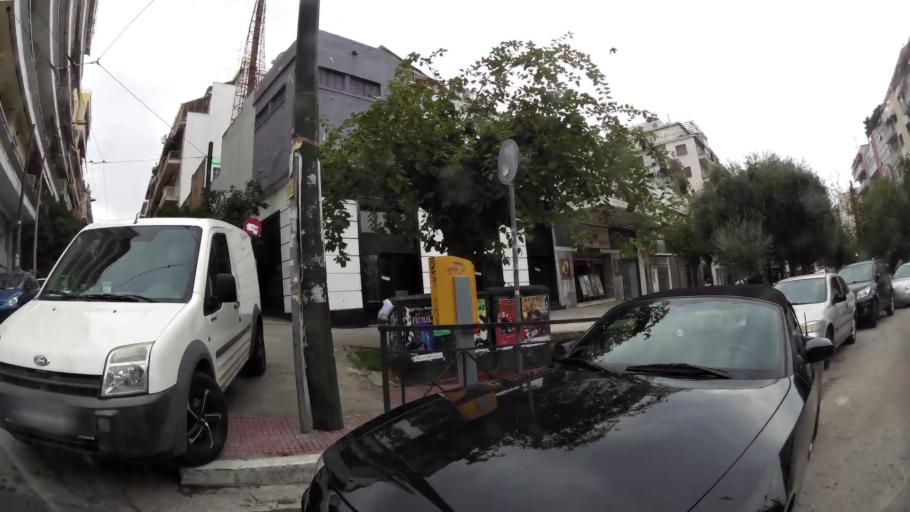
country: GR
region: Attica
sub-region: Nomarchia Athinas
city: Vyronas
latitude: 37.9675
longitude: 23.7501
